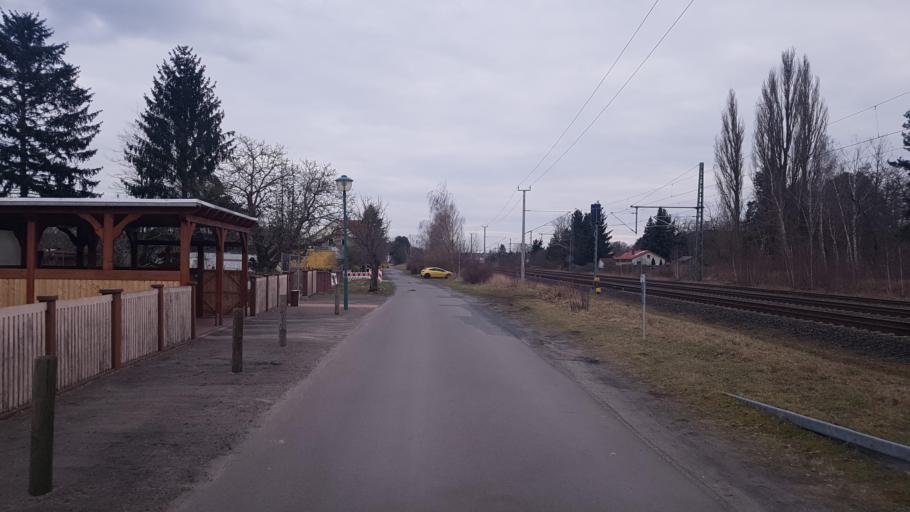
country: DE
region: Brandenburg
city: Halbe
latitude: 52.1137
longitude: 13.6963
